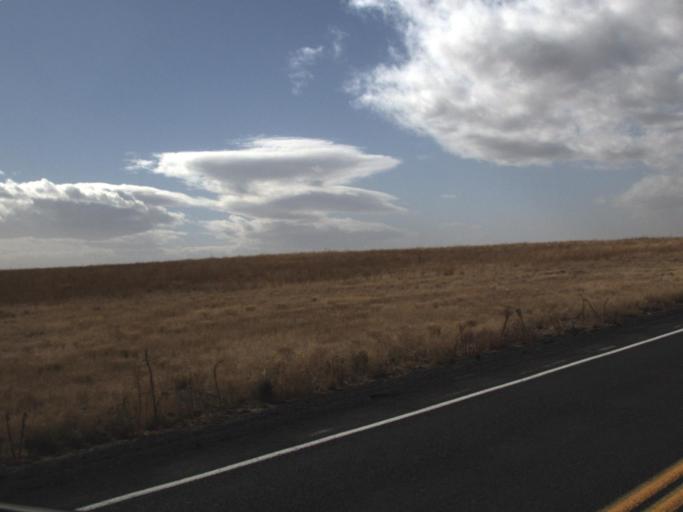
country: US
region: Washington
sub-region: Okanogan County
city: Coulee Dam
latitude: 47.6125
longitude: -118.7506
